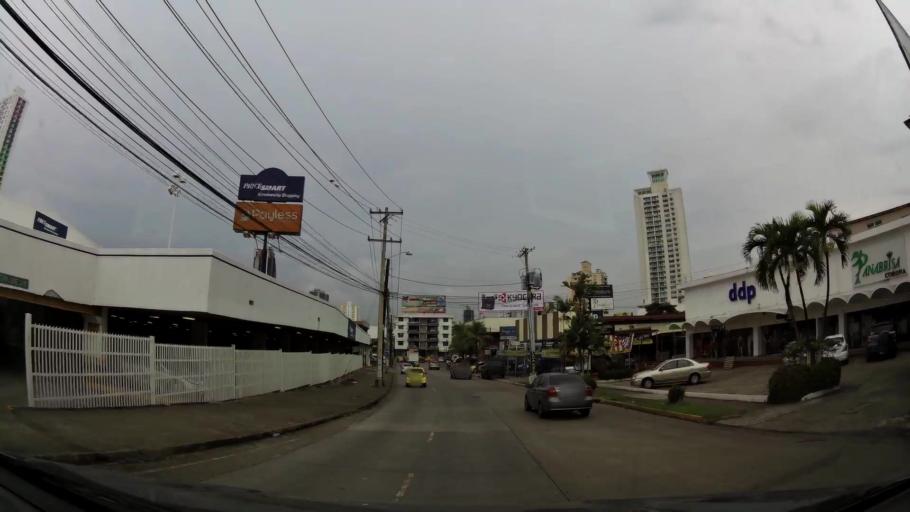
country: PA
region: Panama
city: Panama
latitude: 8.9913
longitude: -79.5194
